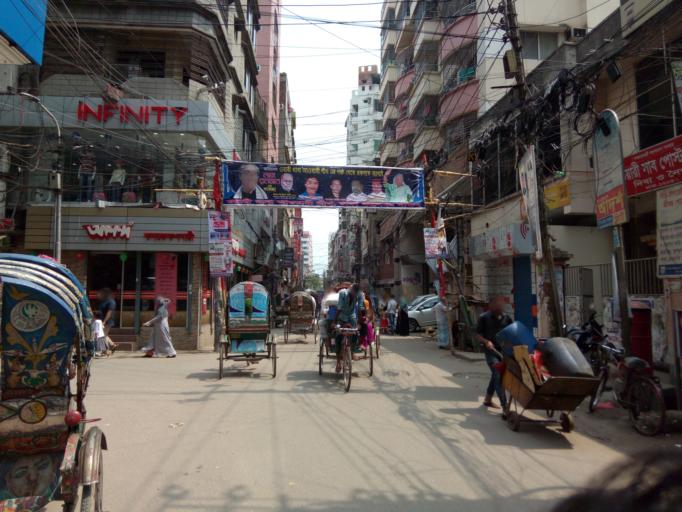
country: BD
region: Dhaka
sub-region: Dhaka
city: Dhaka
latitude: 23.7204
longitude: 90.4165
